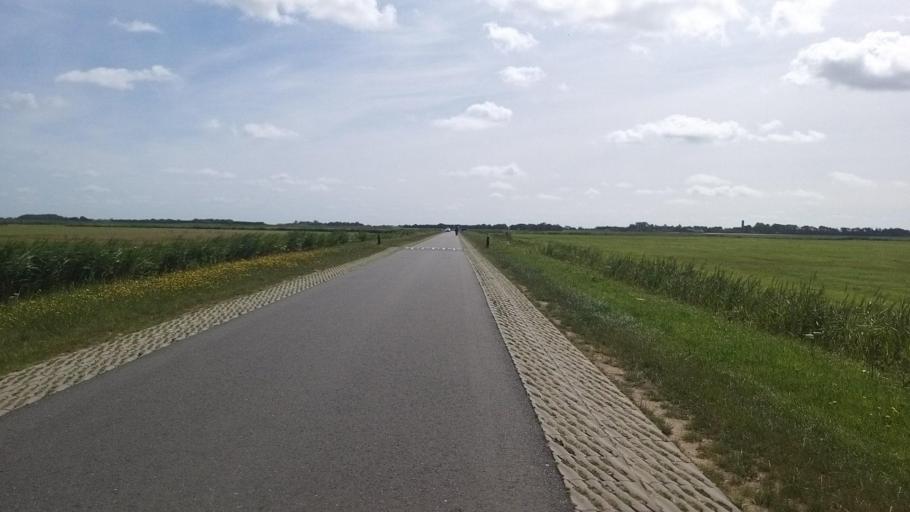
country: NL
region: North Holland
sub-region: Gemeente Texel
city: Den Burg
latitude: 53.0826
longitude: 4.8024
